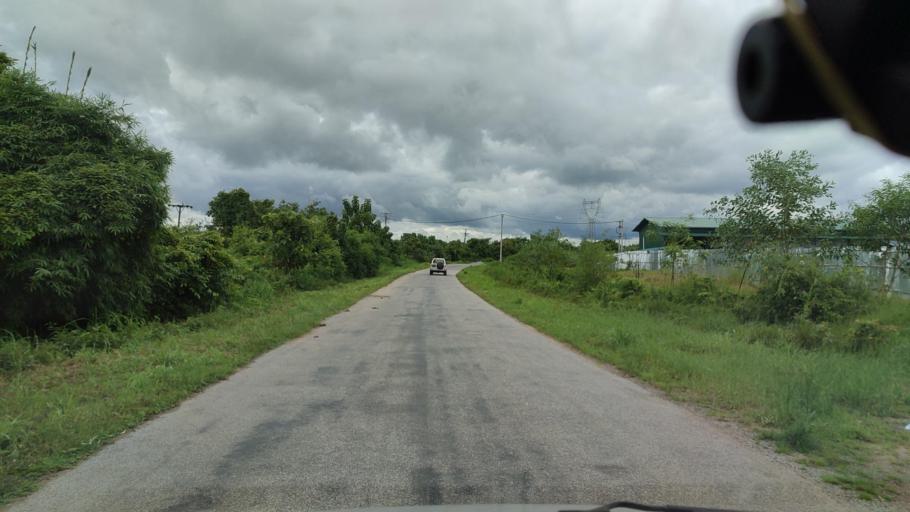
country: MM
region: Bago
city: Bago
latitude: 17.2542
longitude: 96.4172
